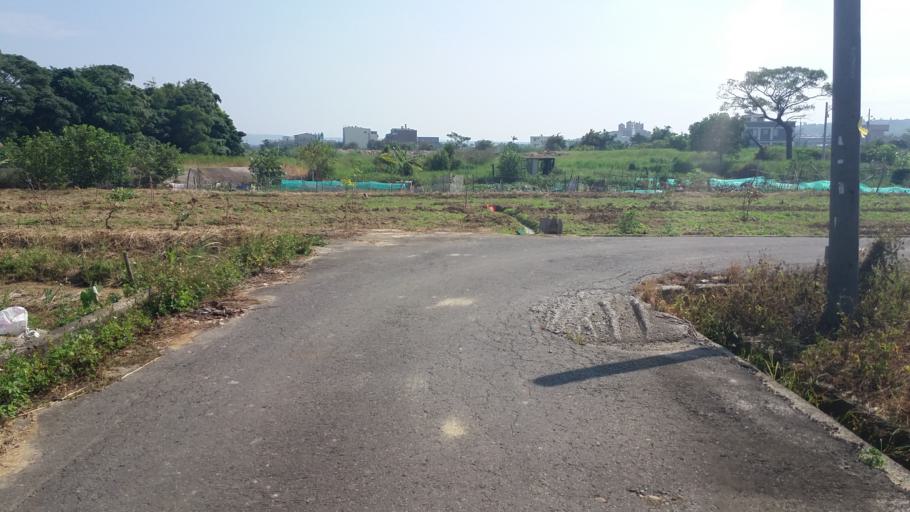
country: TW
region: Taiwan
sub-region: Hsinchu
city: Zhubei
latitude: 24.8962
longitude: 121.0165
